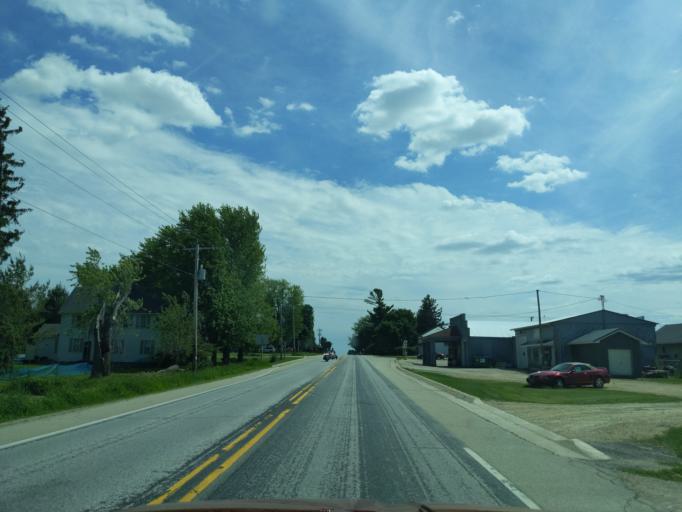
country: US
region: Wisconsin
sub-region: Dane County
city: De Forest
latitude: 43.3111
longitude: -89.3254
